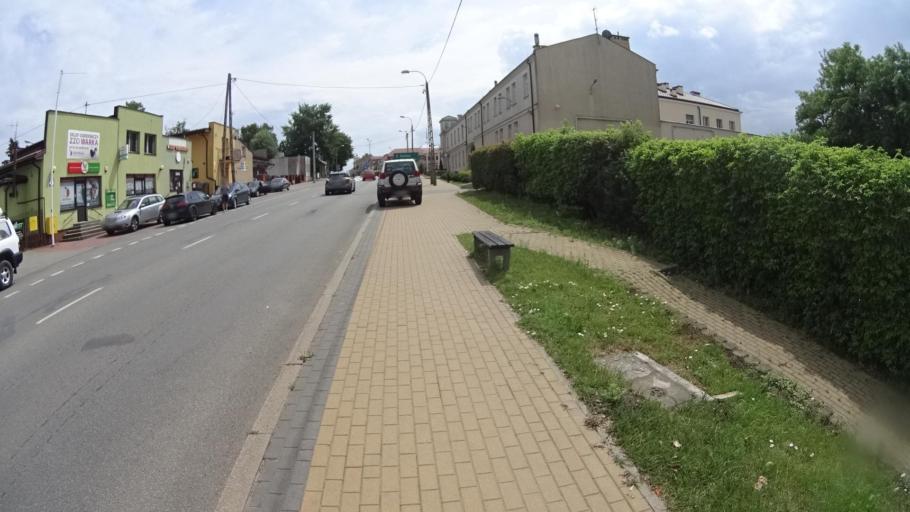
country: PL
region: Masovian Voivodeship
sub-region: Powiat grojecki
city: Grojec
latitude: 51.8695
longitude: 20.8651
